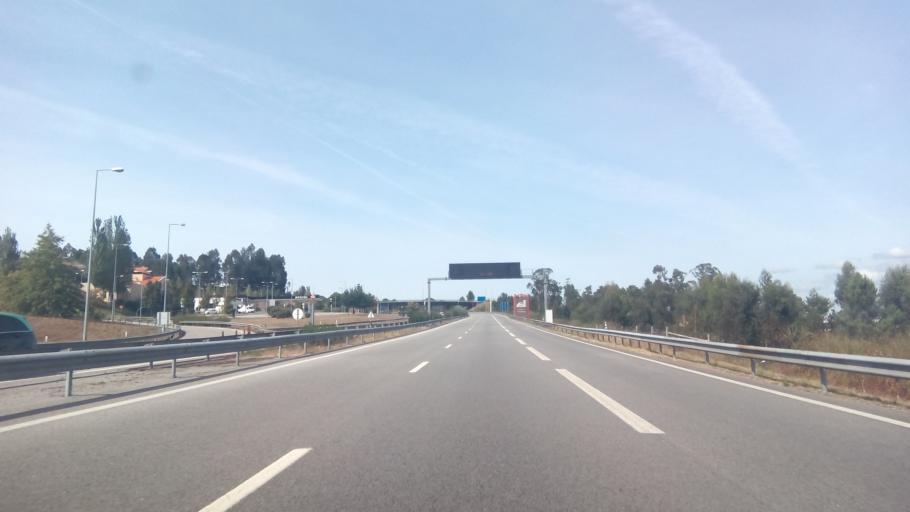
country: PT
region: Porto
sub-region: Marco de Canaveses
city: Marco de Canavezes
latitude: 41.2309
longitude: -8.1766
